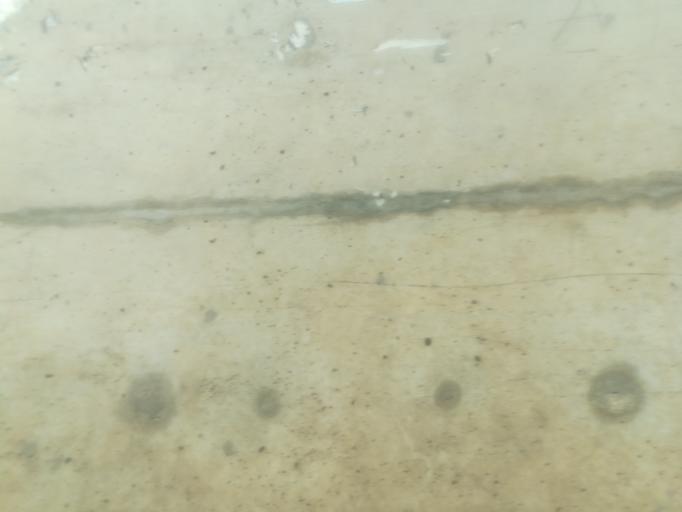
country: NG
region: Kano
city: Kano
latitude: 12.0120
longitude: 8.5347
